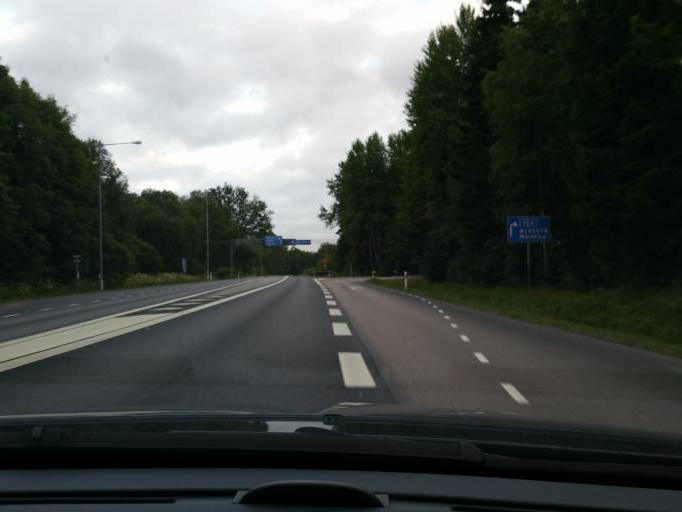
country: SE
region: Kronoberg
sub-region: Vaxjo Kommun
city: Lammhult
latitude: 57.0913
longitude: 14.6403
